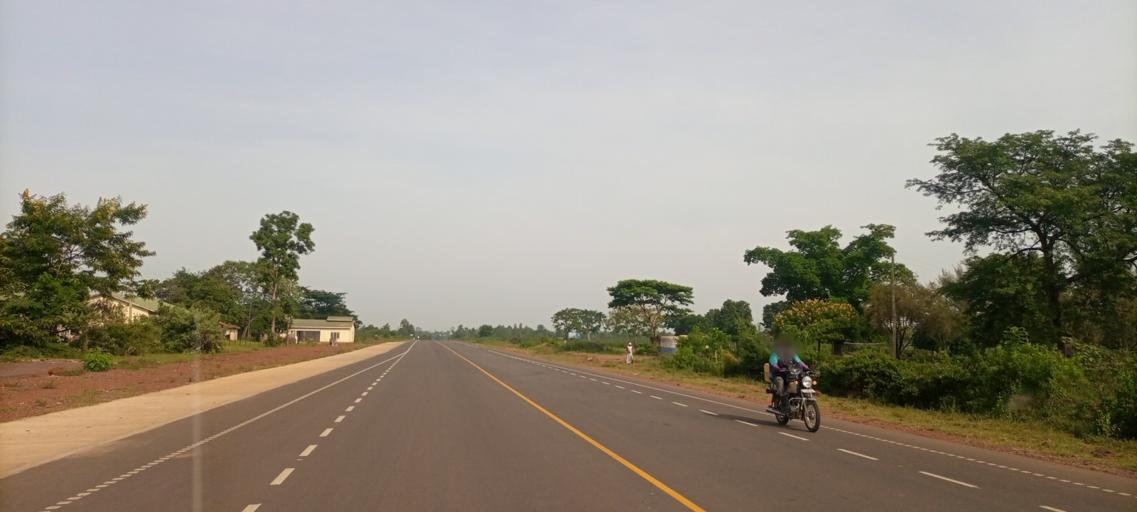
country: UG
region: Eastern Region
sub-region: Budaka District
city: Budaka
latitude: 1.1012
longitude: 34.0036
